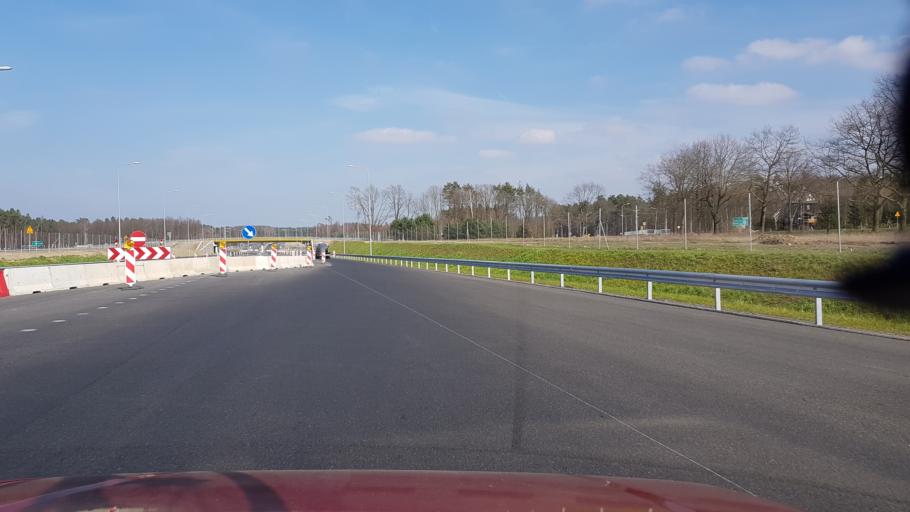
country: PL
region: West Pomeranian Voivodeship
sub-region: Powiat goleniowski
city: Osina
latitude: 53.6298
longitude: 14.9909
